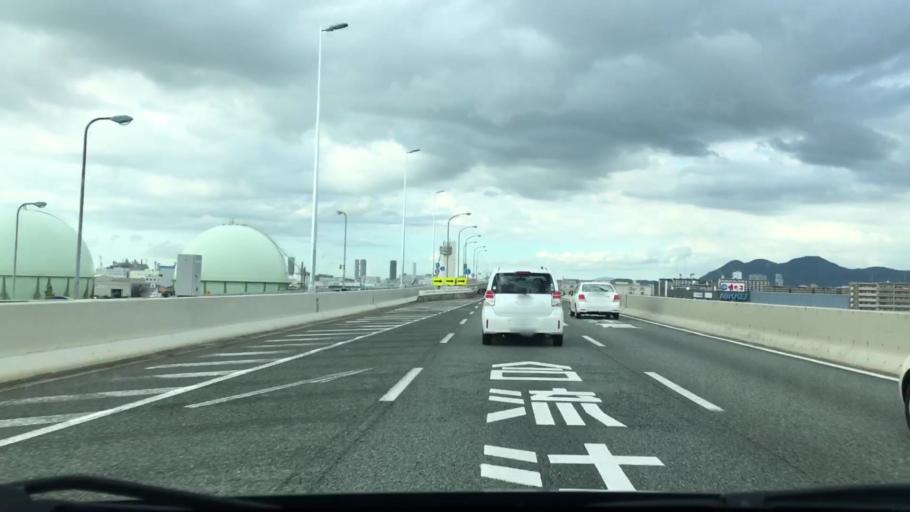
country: JP
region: Fukuoka
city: Fukuoka-shi
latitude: 33.6148
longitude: 130.4106
